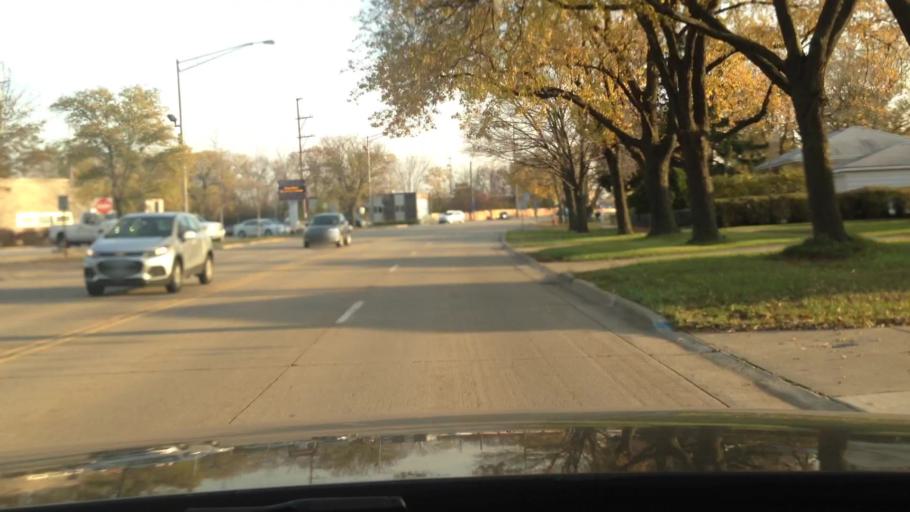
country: US
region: Illinois
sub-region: Cook County
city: Schiller Park
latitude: 41.9614
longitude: -87.8722
